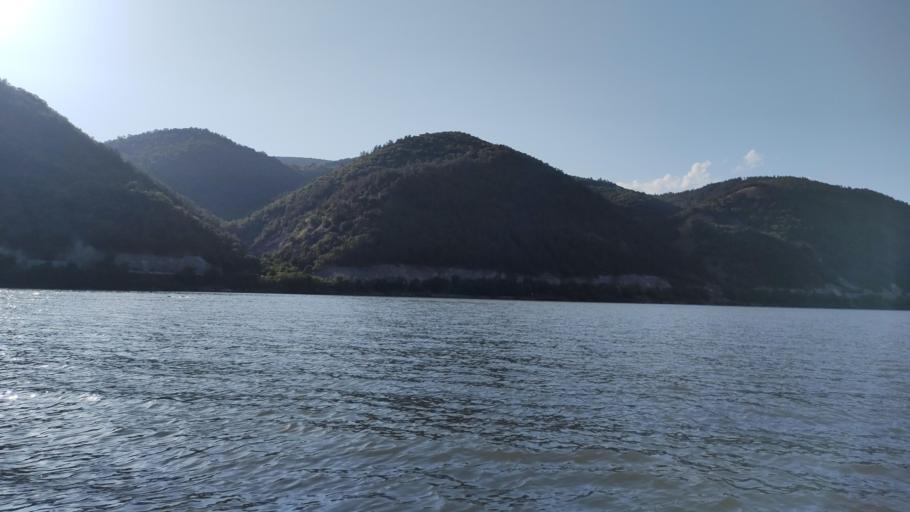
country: RO
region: Mehedinti
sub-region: Comuna Svinita
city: Svinita
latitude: 44.4998
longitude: 22.1914
